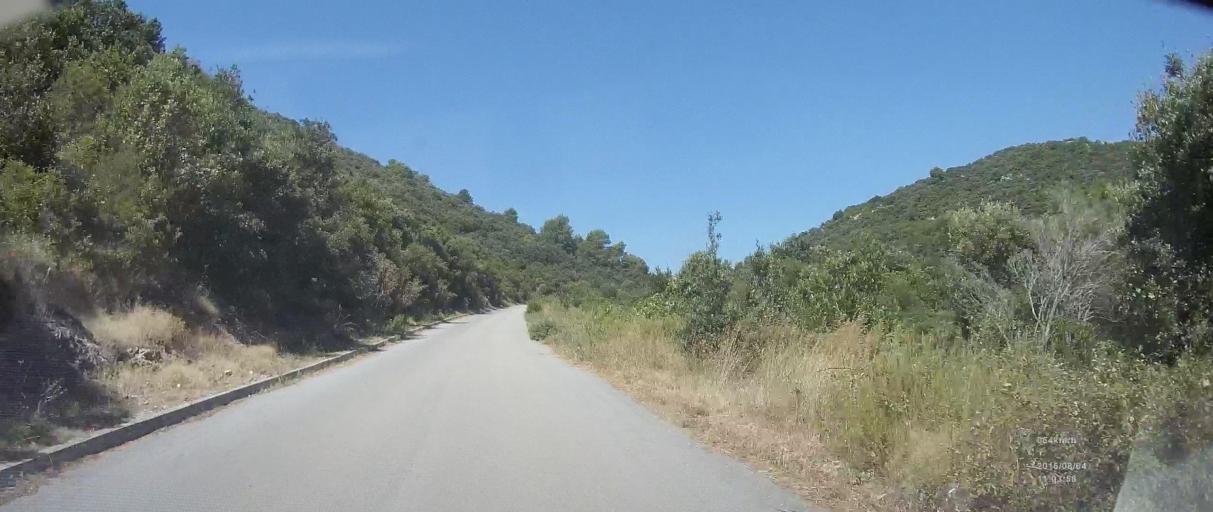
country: HR
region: Dubrovacko-Neretvanska
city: Blato
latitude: 42.7765
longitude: 17.4582
